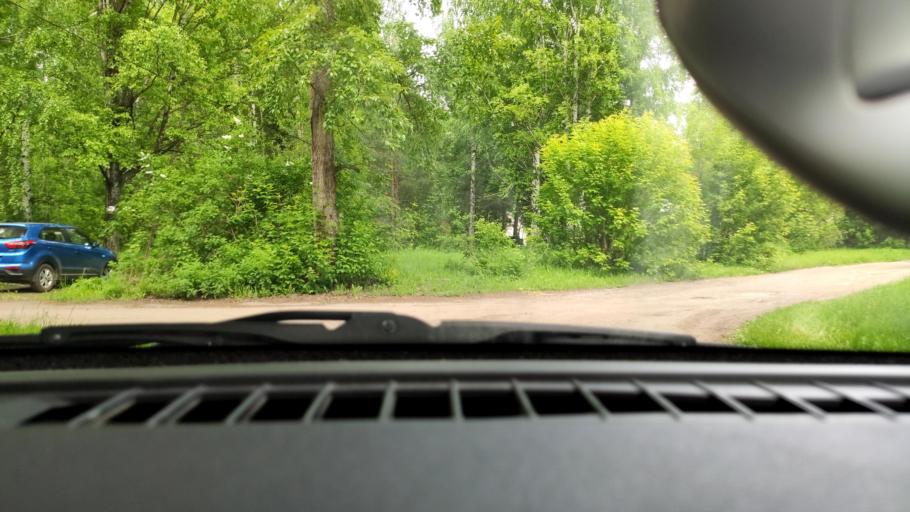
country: RU
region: Perm
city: Kondratovo
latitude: 57.9764
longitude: 56.1466
